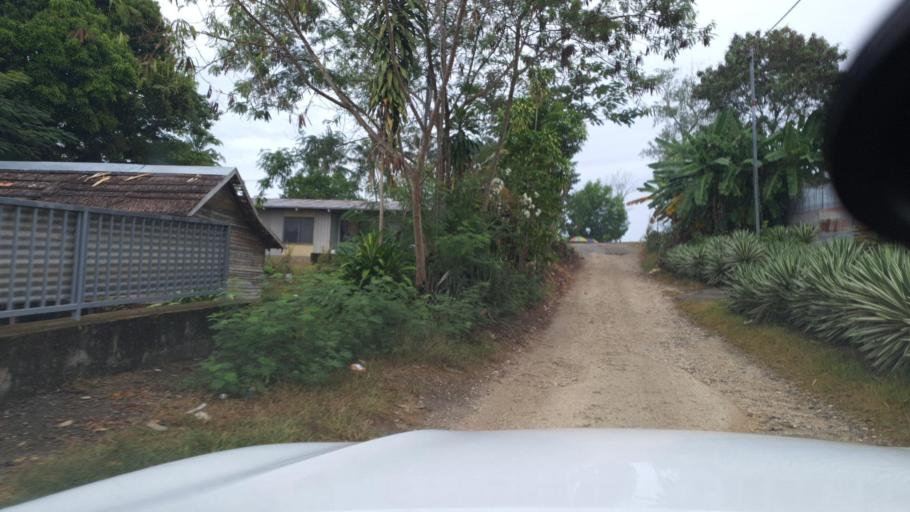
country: SB
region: Guadalcanal
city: Honiara
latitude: -9.4427
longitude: 159.9665
